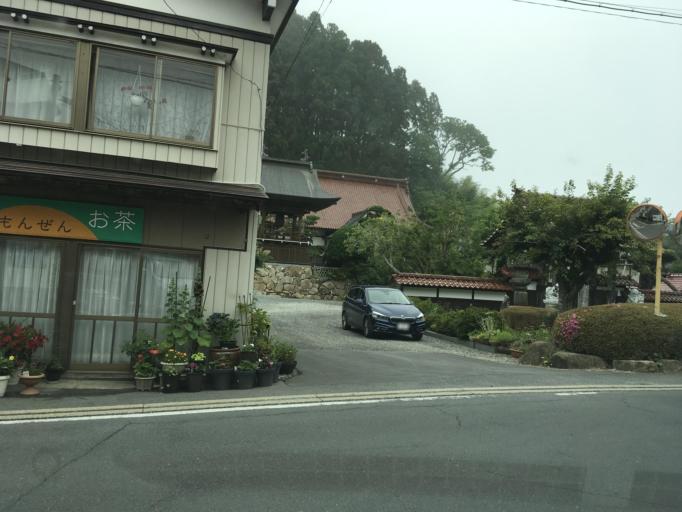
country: JP
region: Iwate
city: Ofunato
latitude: 38.9021
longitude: 141.6461
